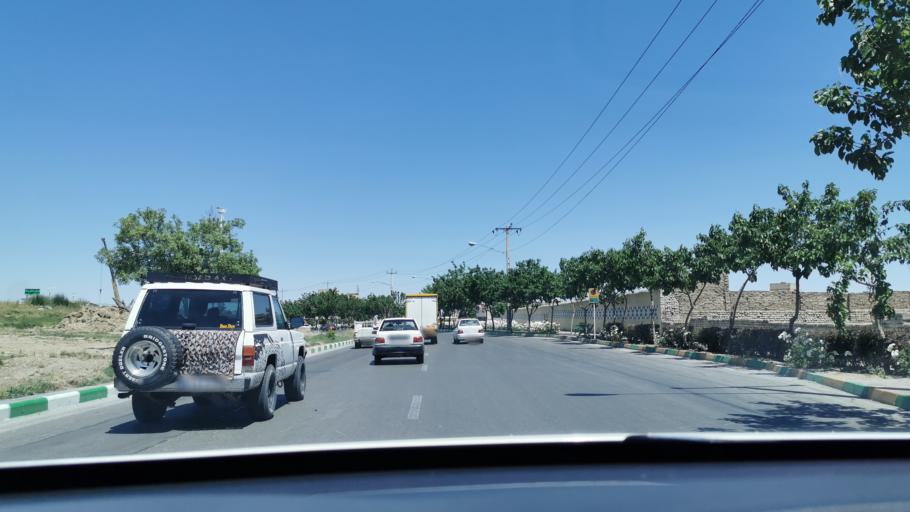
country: IR
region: Razavi Khorasan
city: Mashhad
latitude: 36.2591
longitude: 59.6452
